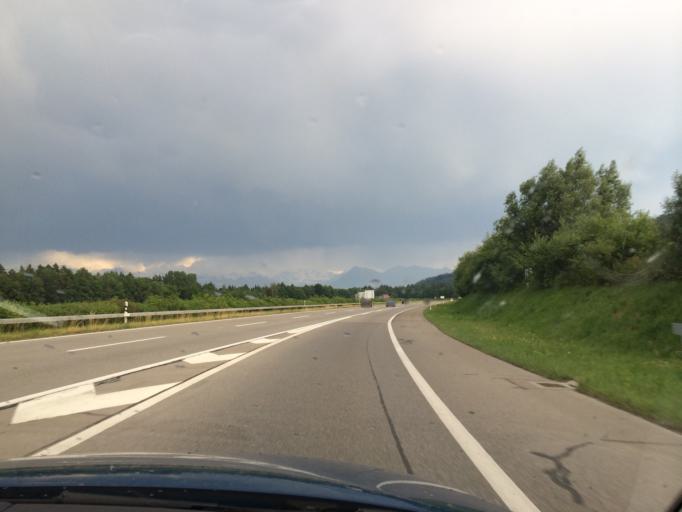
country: CH
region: Bern
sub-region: Bern-Mittelland District
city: Rubigen
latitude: 46.8883
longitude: 7.5401
